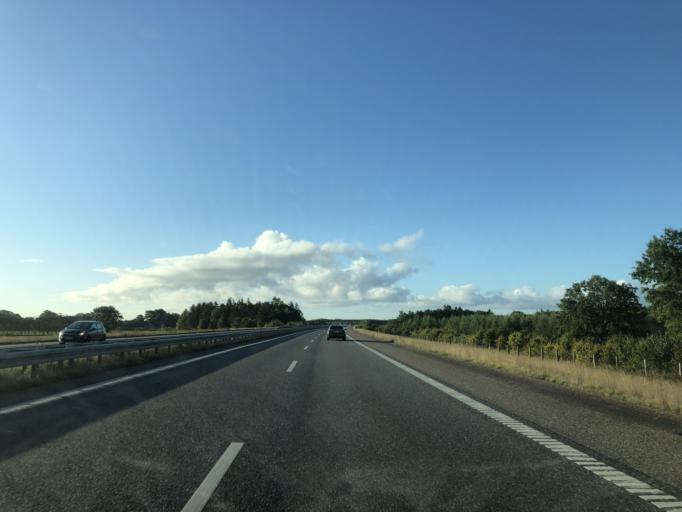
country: DK
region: South Denmark
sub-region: Vejle Kommune
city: Give
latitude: 55.8963
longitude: 9.2149
